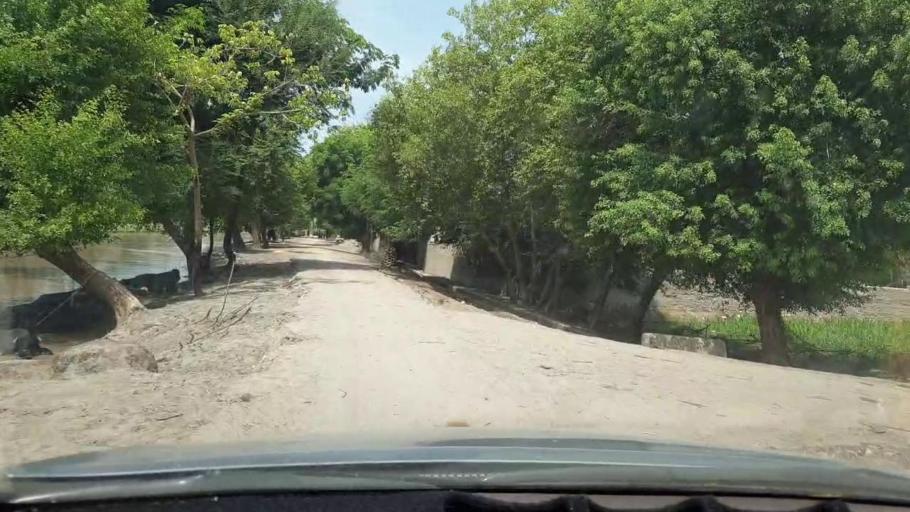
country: PK
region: Sindh
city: Khairpur
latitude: 27.4512
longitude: 68.7982
